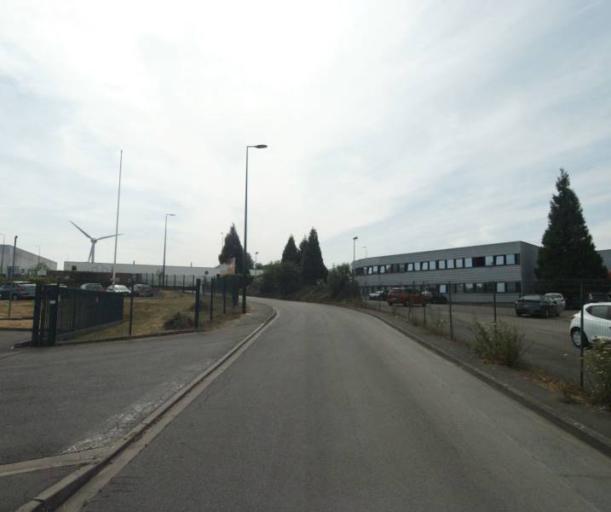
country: FR
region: Nord-Pas-de-Calais
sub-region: Departement du Nord
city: Mouvaux
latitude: 50.7200
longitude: 3.1277
